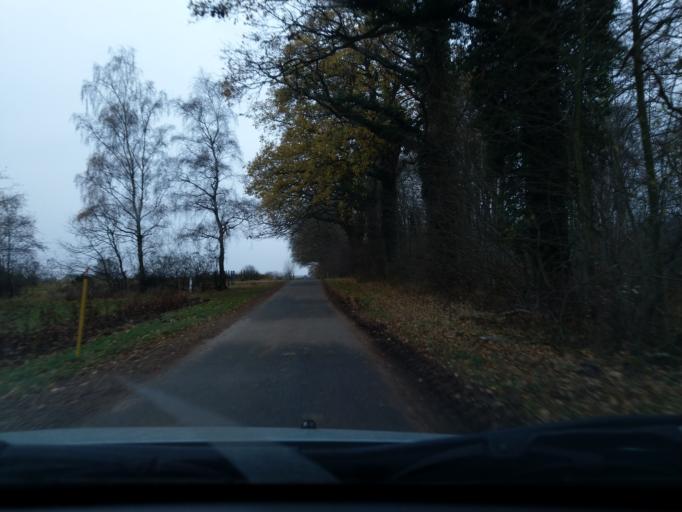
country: DK
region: Zealand
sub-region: Vordingborg Kommune
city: Praesto
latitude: 55.1143
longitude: 12.1447
